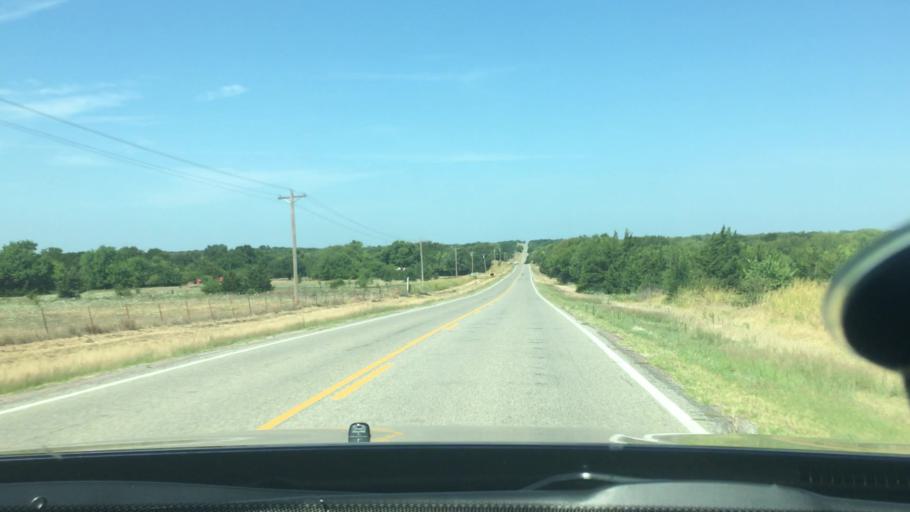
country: US
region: Oklahoma
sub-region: Marshall County
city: Kingston
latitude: 33.9983
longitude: -96.8183
